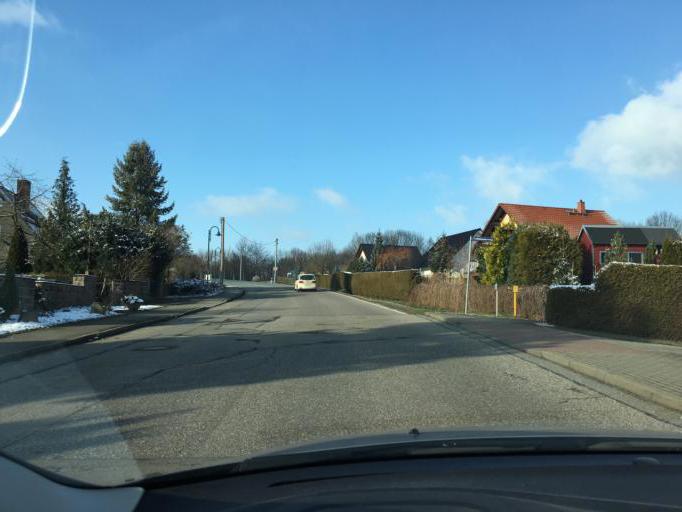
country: DE
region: Saxony
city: Penig
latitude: 50.9383
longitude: 12.6963
